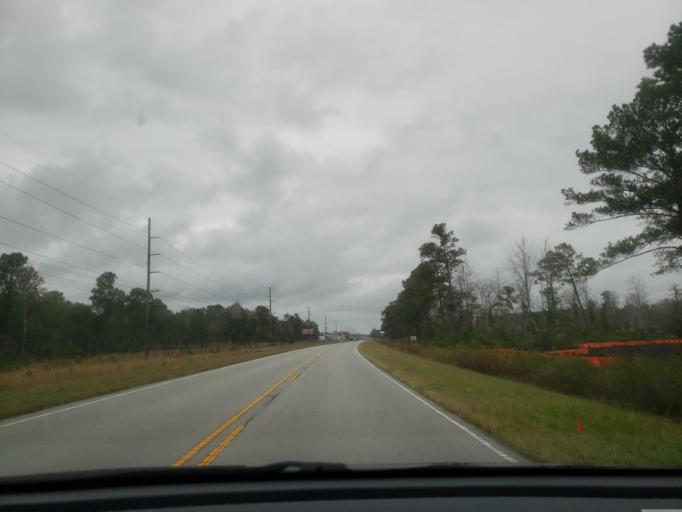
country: US
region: North Carolina
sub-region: Onslow County
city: Sneads Ferry
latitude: 34.5181
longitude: -77.4361
